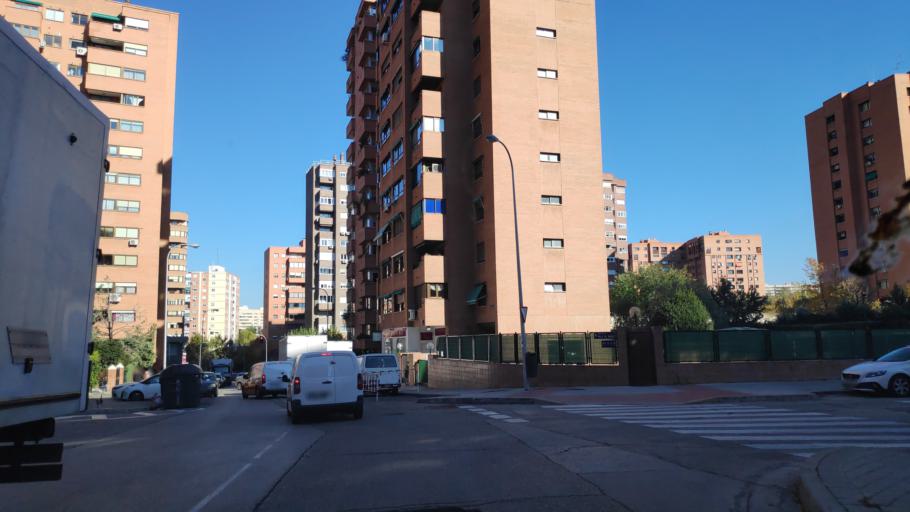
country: ES
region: Madrid
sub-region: Provincia de Madrid
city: Tetuan de las Victorias
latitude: 40.4769
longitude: -3.6990
